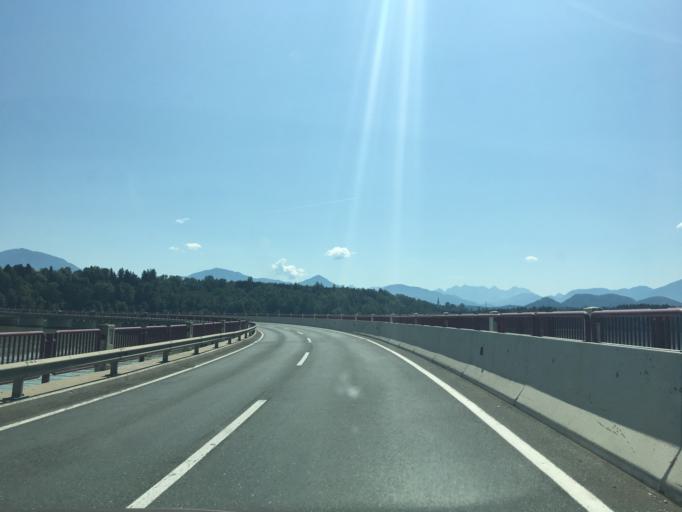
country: AT
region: Carinthia
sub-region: Politischer Bezirk Volkermarkt
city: Voelkermarkt
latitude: 46.6481
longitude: 14.6263
